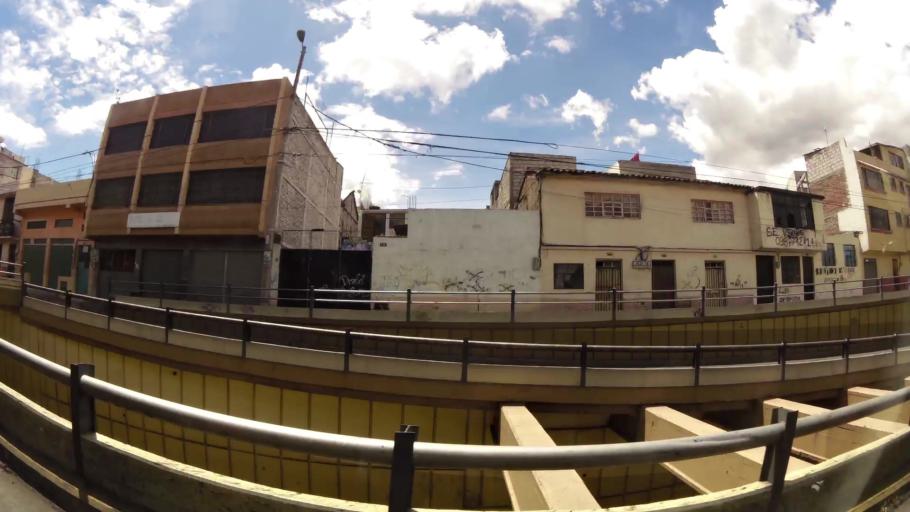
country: EC
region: Tungurahua
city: Ambato
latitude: -1.2482
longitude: -78.6321
